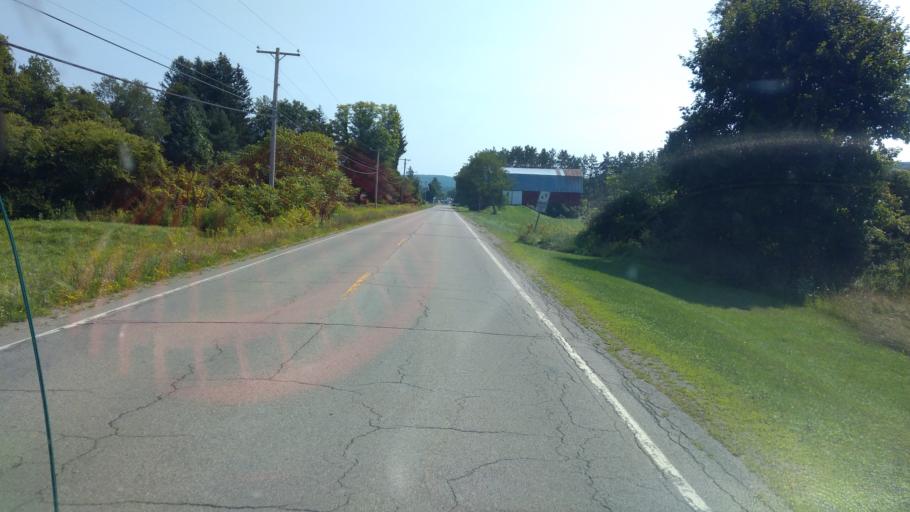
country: US
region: New York
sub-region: Allegany County
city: Friendship
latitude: 42.2014
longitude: -78.1559
